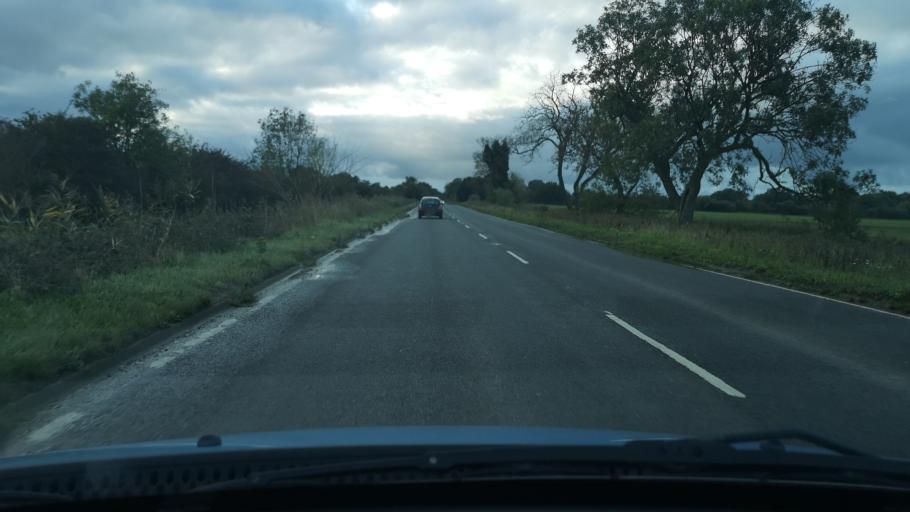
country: GB
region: England
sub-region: North Lincolnshire
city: Belton
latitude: 53.5820
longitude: -0.8005
